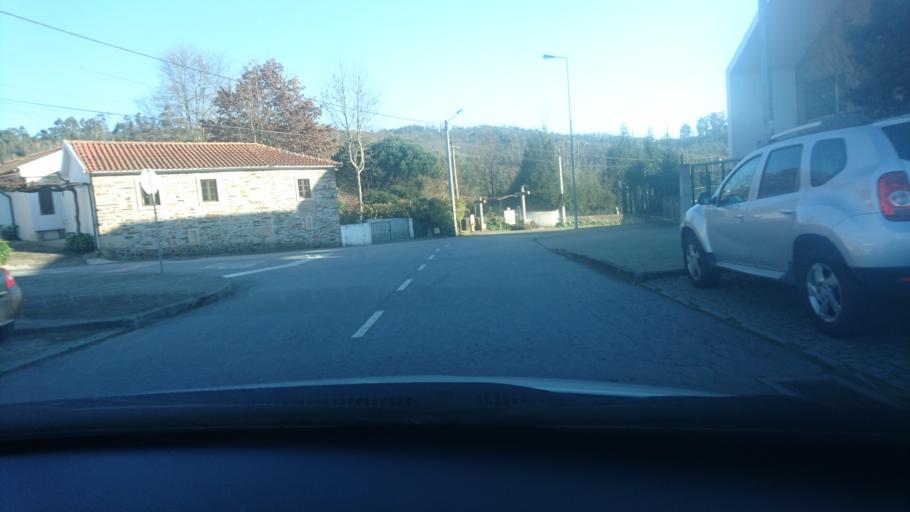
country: PT
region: Porto
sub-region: Paredes
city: Recarei
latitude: 41.1466
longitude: -8.3875
